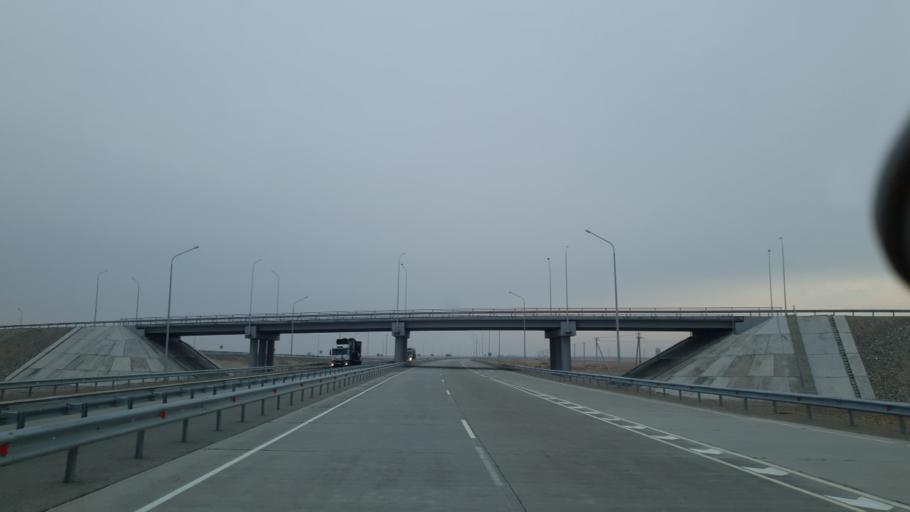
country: KZ
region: Almaty Oblysy
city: Zharkent
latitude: 44.0135
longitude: 79.6737
